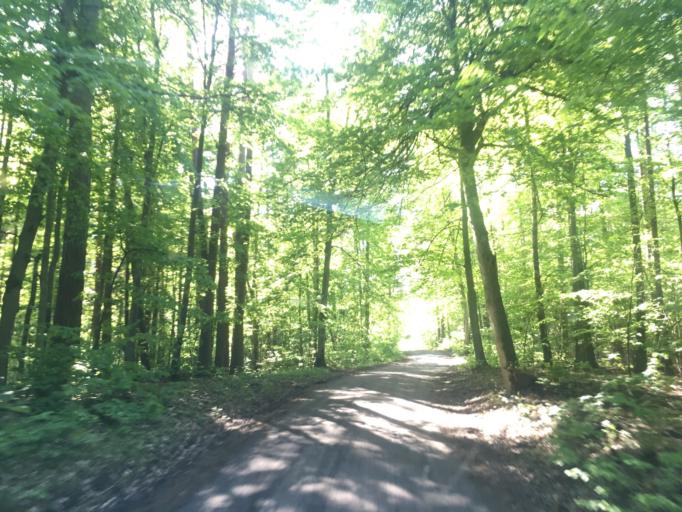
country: PL
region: Warmian-Masurian Voivodeship
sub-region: Powiat mragowski
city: Mikolajki
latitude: 53.7486
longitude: 21.6187
